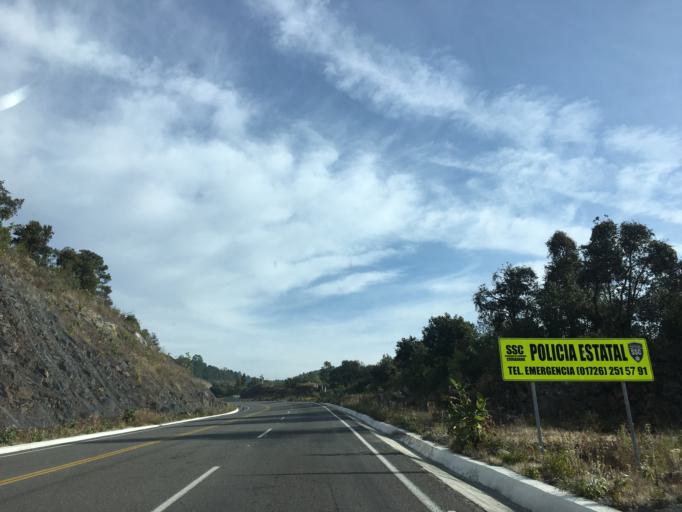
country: MX
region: Mexico
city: San Bartolo
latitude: 19.2588
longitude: -100.0660
